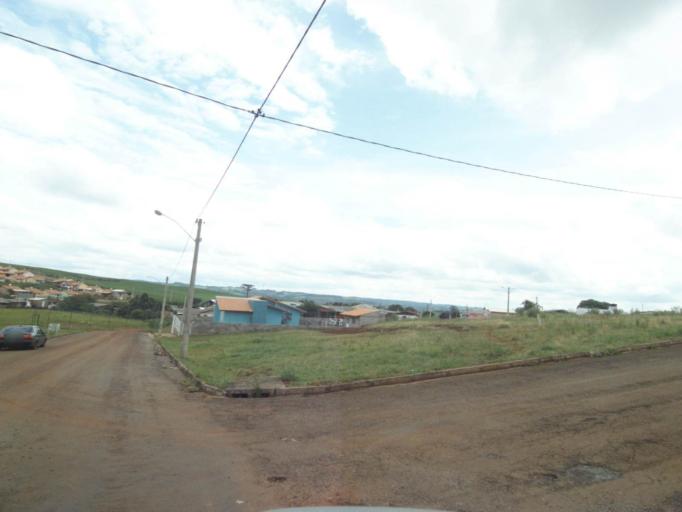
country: BR
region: Rio Grande do Sul
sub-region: Lagoa Vermelha
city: Lagoa Vermelha
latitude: -28.2219
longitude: -51.5182
